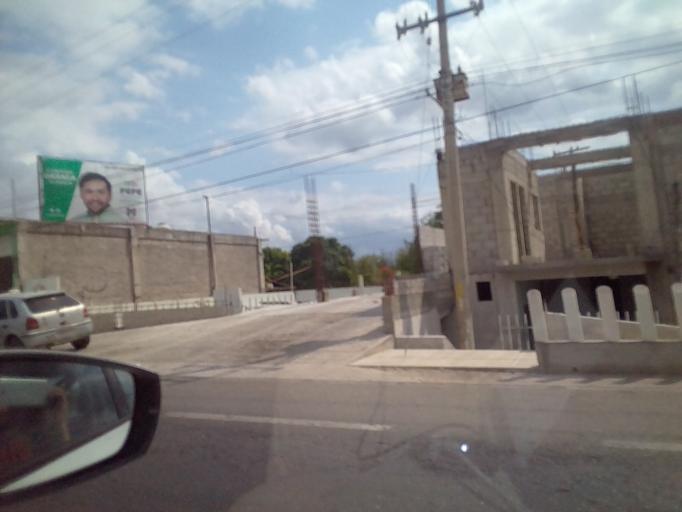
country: MX
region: Oaxaca
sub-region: Santo Domingo Tehuantepec
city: Santo Domingo Tehuantepec
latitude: 16.3109
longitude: -95.2363
